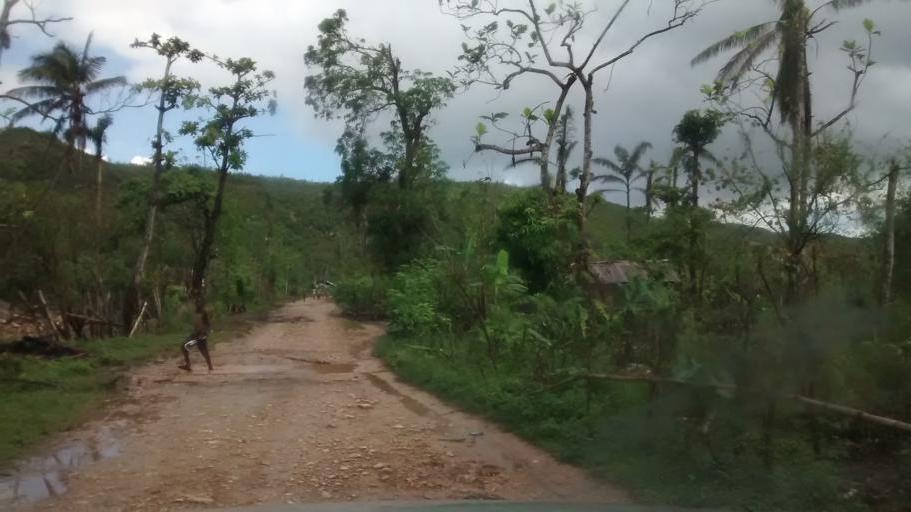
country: HT
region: Grandans
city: Corail
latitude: 18.5362
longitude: -73.9369
